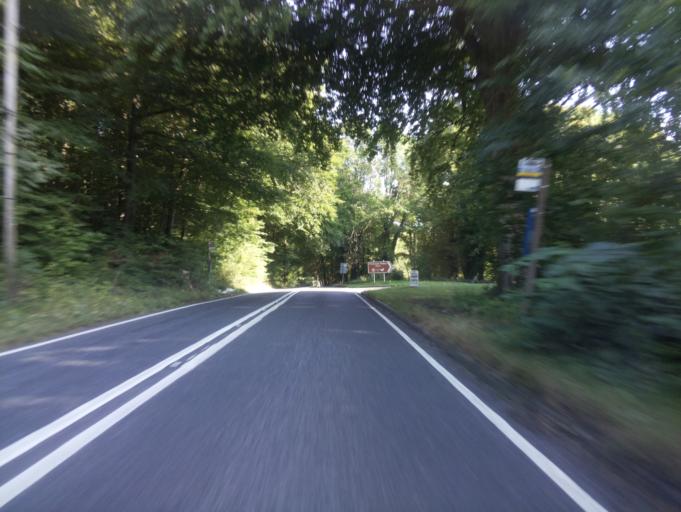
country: GB
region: England
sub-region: Gloucestershire
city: Painswick
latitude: 51.8220
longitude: -2.1697
